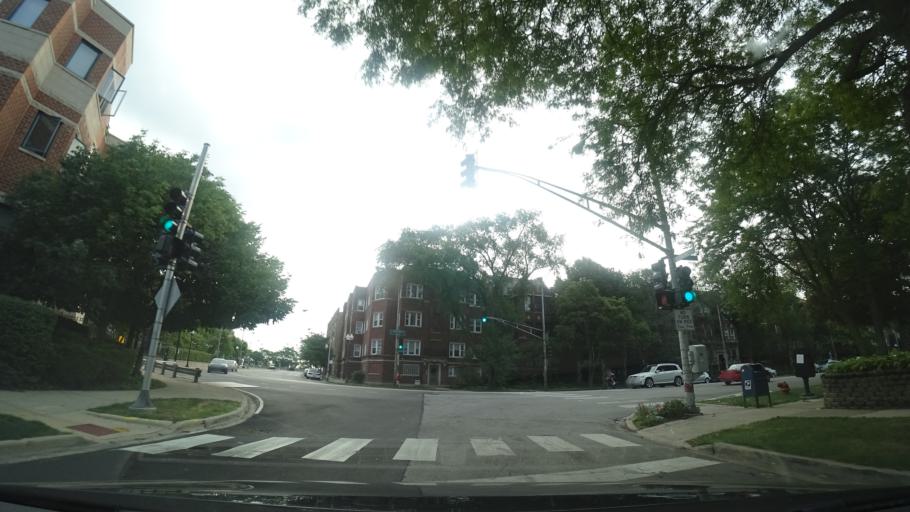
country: US
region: Illinois
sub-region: Cook County
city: Evanston
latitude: 42.0223
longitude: -87.6673
